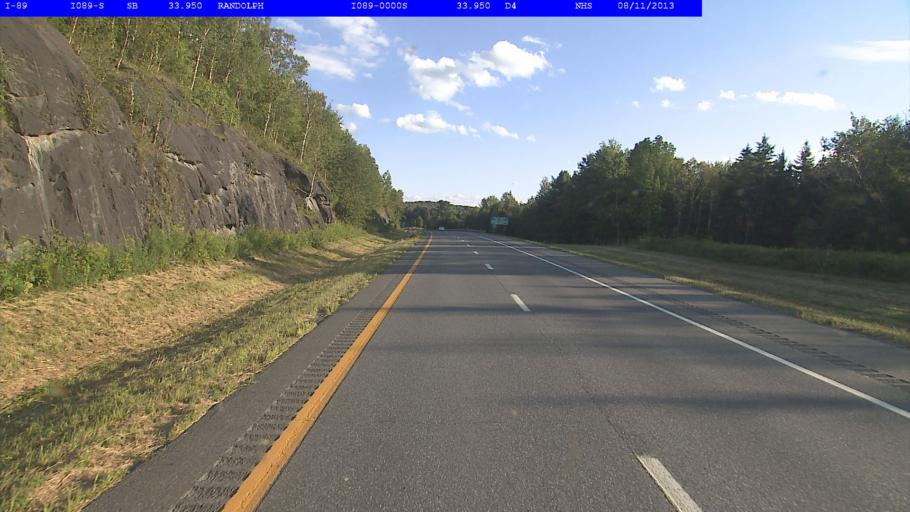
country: US
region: Vermont
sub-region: Orange County
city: Randolph
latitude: 43.9891
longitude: -72.6278
